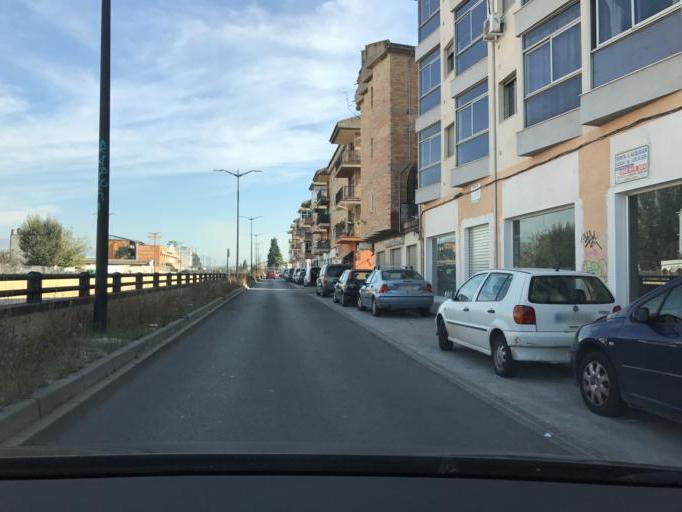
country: ES
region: Andalusia
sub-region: Provincia de Granada
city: Atarfe
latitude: 37.1923
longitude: -3.7119
